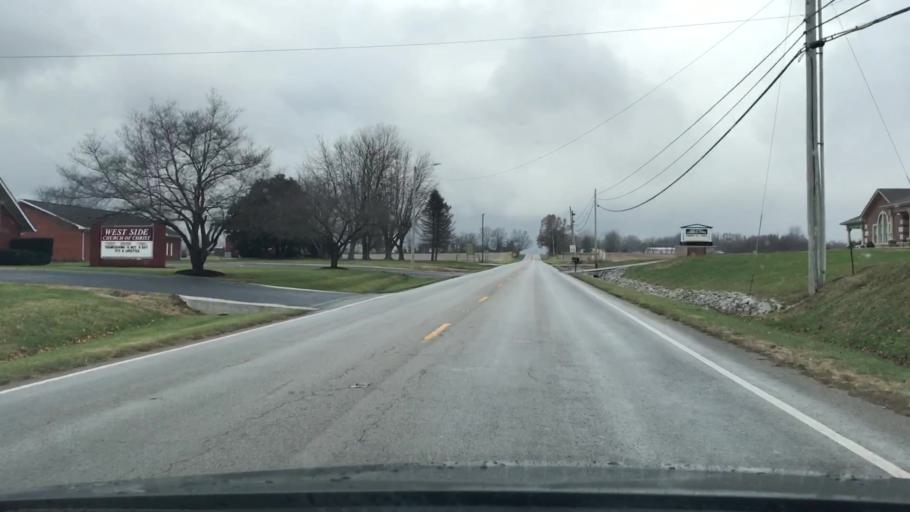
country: US
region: Kentucky
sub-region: Todd County
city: Elkton
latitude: 36.8145
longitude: -87.1754
